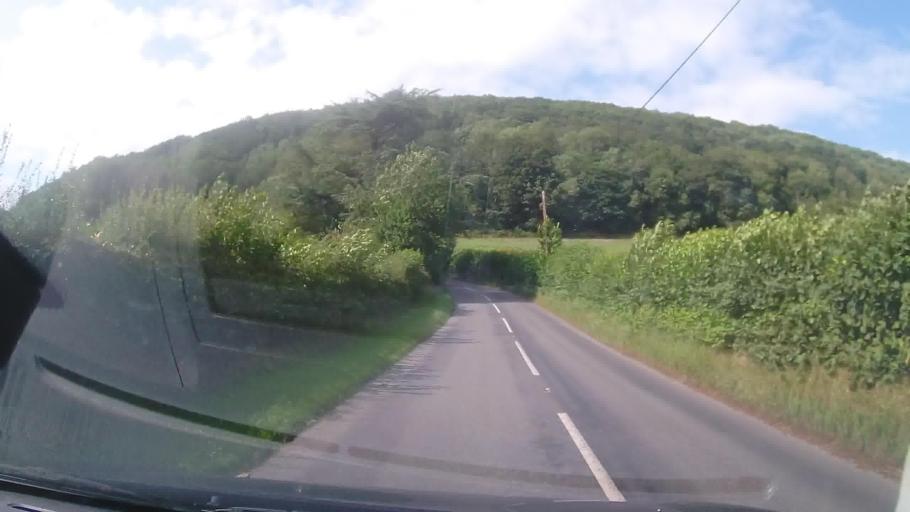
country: GB
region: Wales
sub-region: Sir Powys
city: Knighton
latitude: 52.3509
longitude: -3.0276
